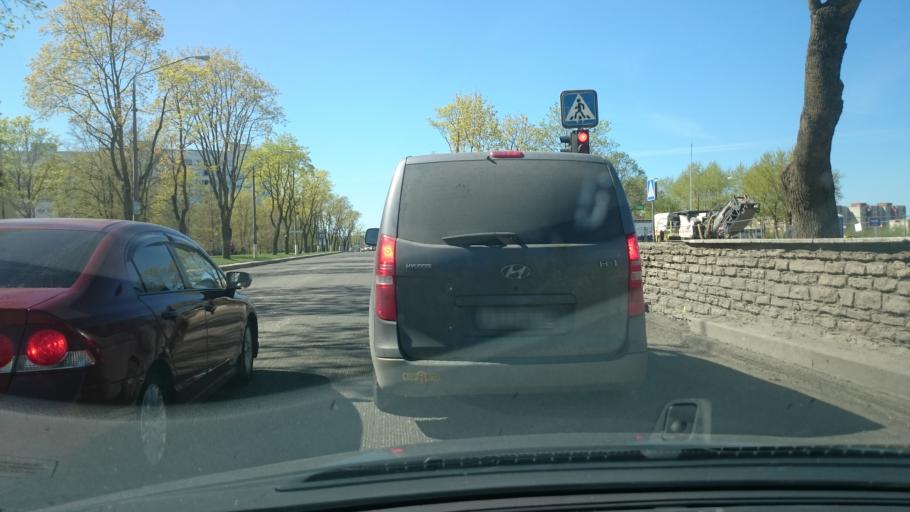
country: EE
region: Ida-Virumaa
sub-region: Narva linn
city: Narva
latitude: 59.3817
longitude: 28.1704
